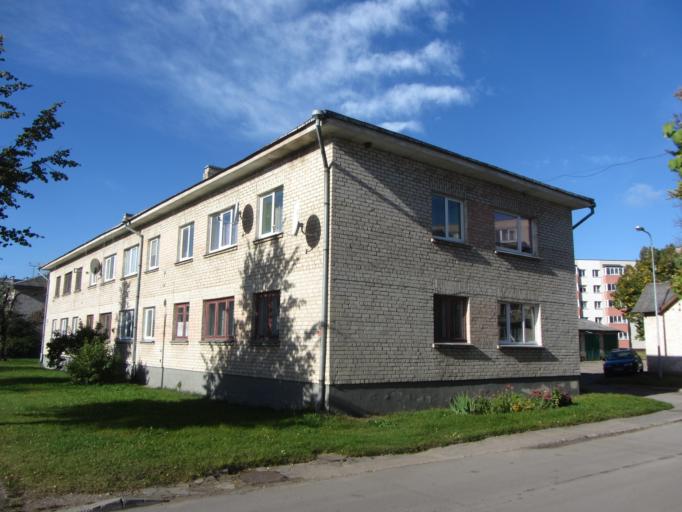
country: LT
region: Utenos apskritis
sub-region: Utena
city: Utena
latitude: 55.5027
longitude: 25.6174
